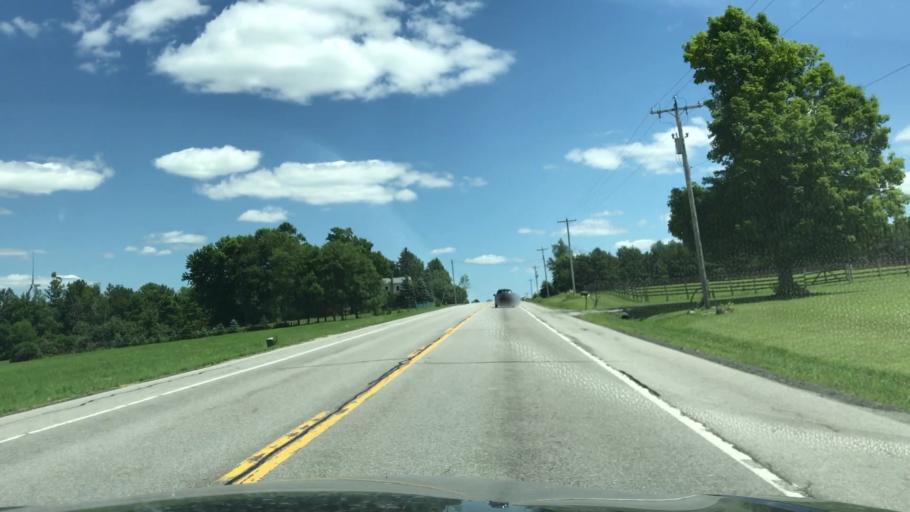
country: US
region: New York
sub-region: Wyoming County
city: Attica
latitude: 42.7549
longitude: -78.2728
